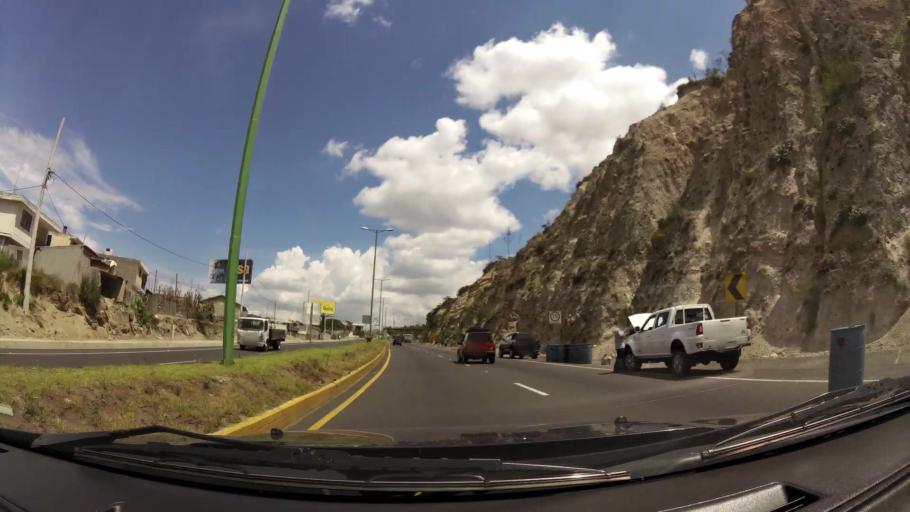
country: EC
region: Pichincha
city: Quito
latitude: -0.0906
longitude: -78.4109
